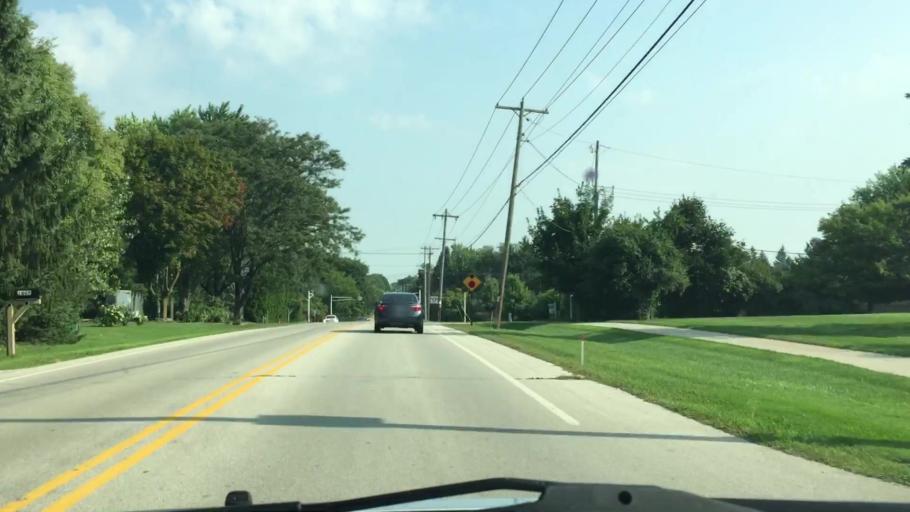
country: US
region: Wisconsin
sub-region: Waukesha County
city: Brookfield
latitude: 43.0525
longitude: -88.1462
